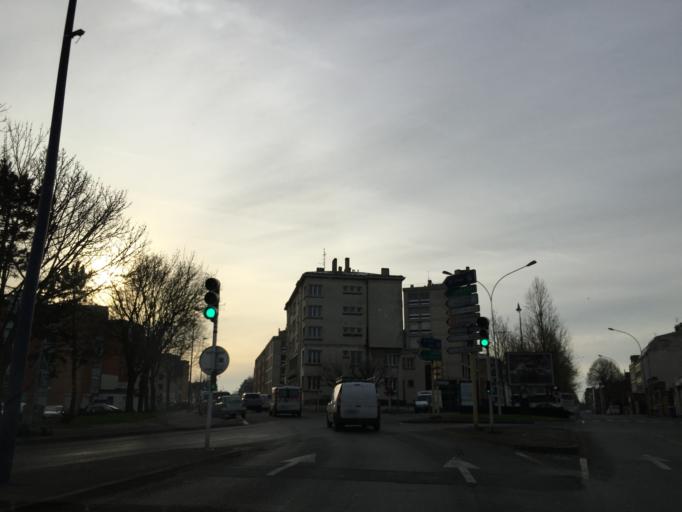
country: FR
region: Nord-Pas-de-Calais
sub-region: Departement du Pas-de-Calais
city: Arras
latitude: 50.2928
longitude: 2.7825
